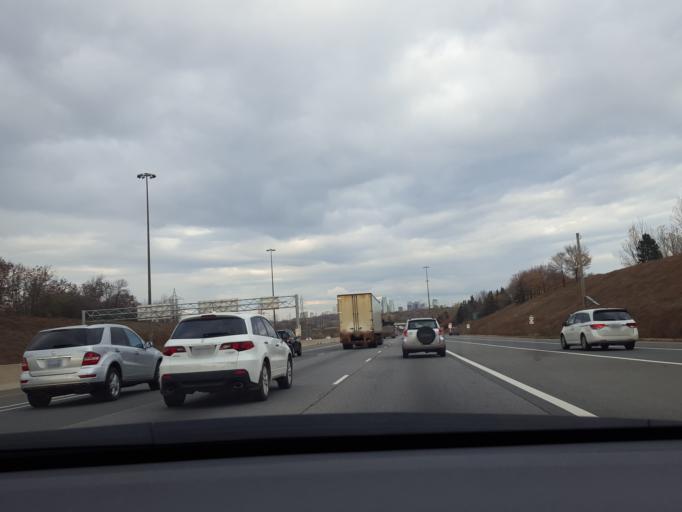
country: CA
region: Ontario
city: Mississauga
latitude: 43.5560
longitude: -79.6933
